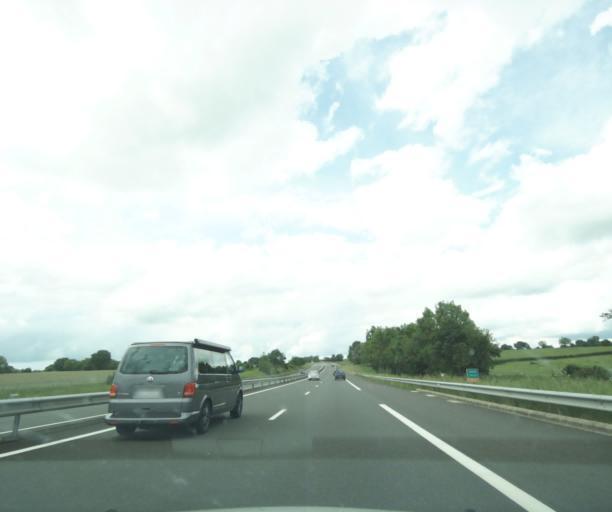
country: FR
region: Auvergne
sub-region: Departement de l'Allier
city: Bellenaves
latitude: 46.2834
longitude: 3.0476
